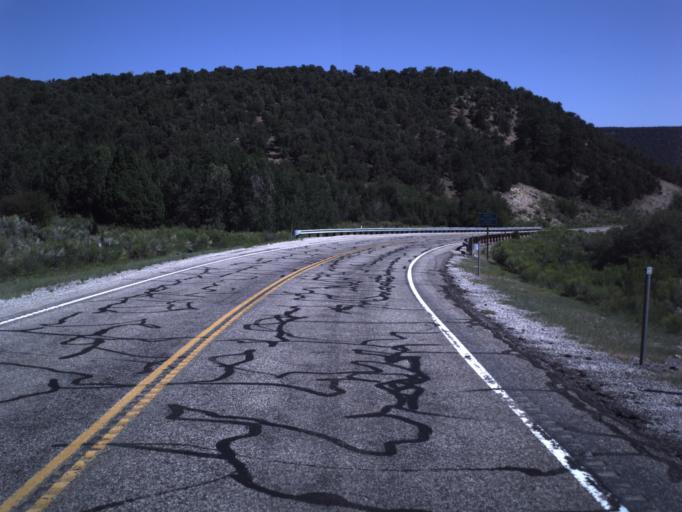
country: US
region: Utah
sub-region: Wayne County
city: Loa
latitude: 38.6562
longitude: -111.4338
